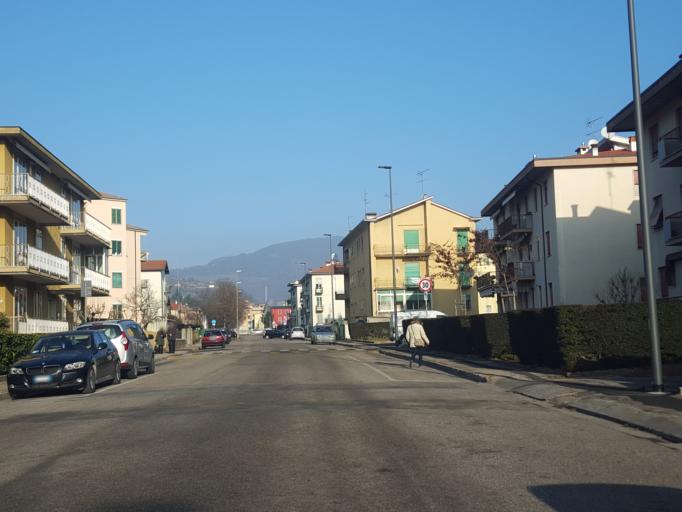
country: IT
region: Veneto
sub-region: Provincia di Vicenza
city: Valdagno
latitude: 45.6359
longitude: 11.3055
